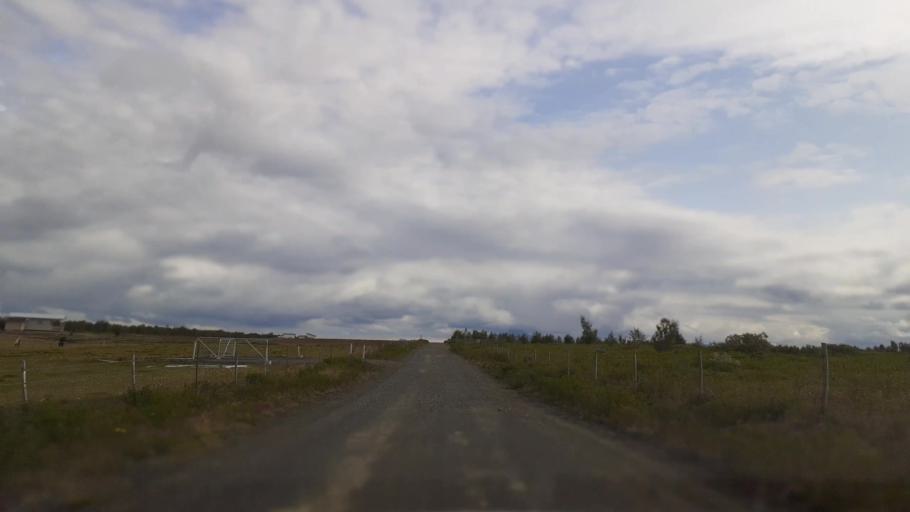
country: IS
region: South
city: Vestmannaeyjar
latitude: 63.8200
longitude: -20.3756
